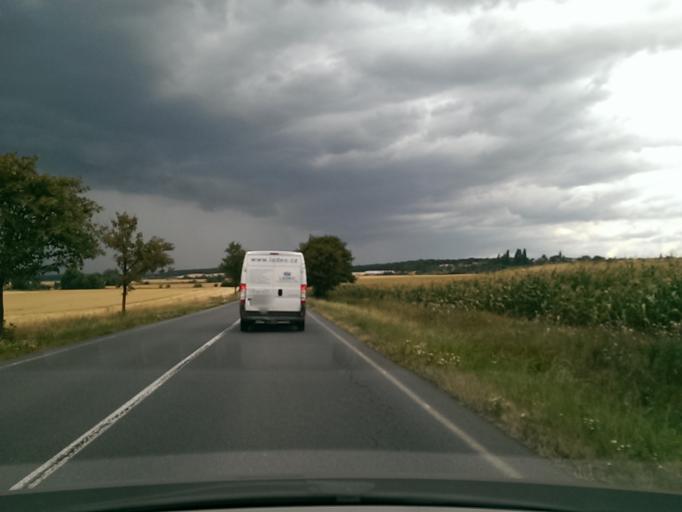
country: CZ
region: Central Bohemia
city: Loucen
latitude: 50.2469
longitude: 15.0060
